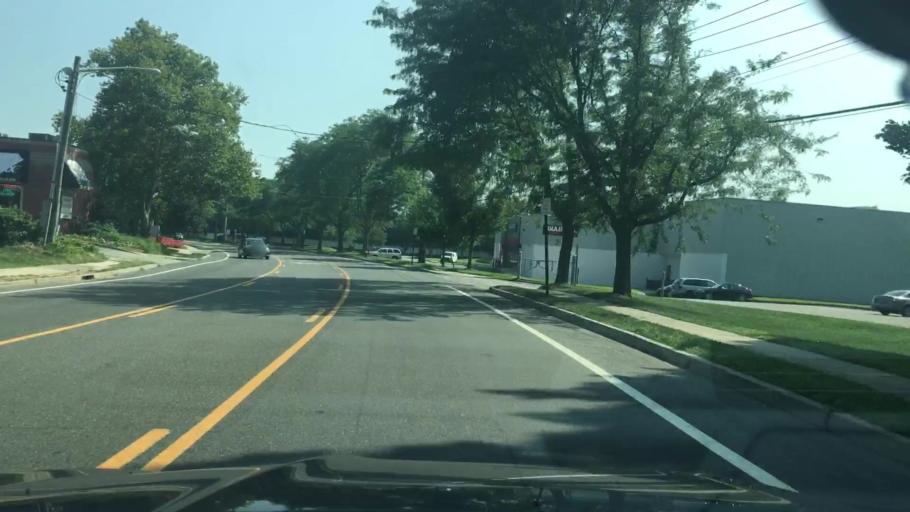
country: US
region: New York
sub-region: Suffolk County
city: Melville
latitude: 40.7710
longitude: -73.4284
